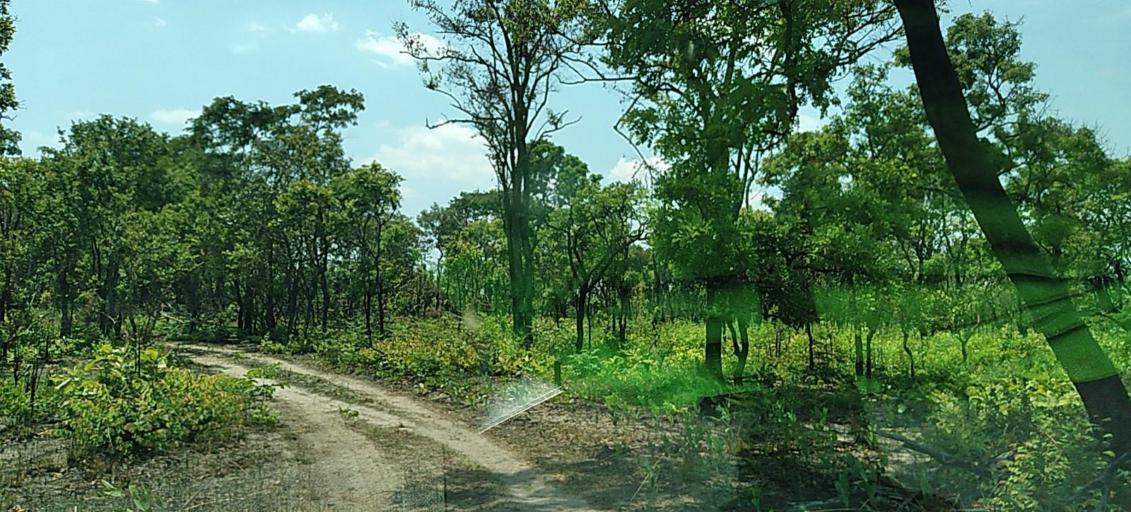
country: CD
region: Katanga
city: Kolwezi
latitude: -11.3023
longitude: 25.2312
